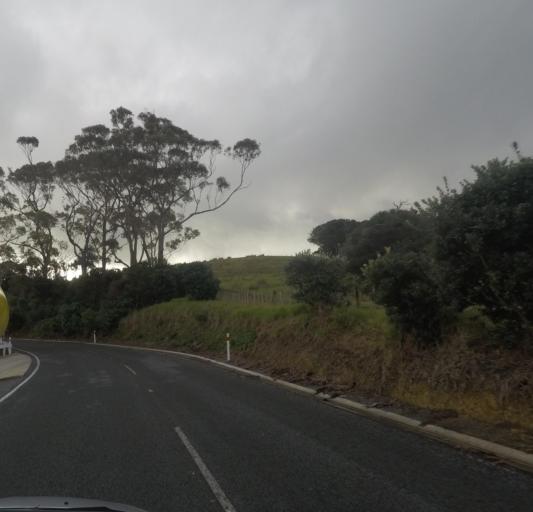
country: NZ
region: Auckland
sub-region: Auckland
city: Warkworth
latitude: -36.3761
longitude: 174.8130
